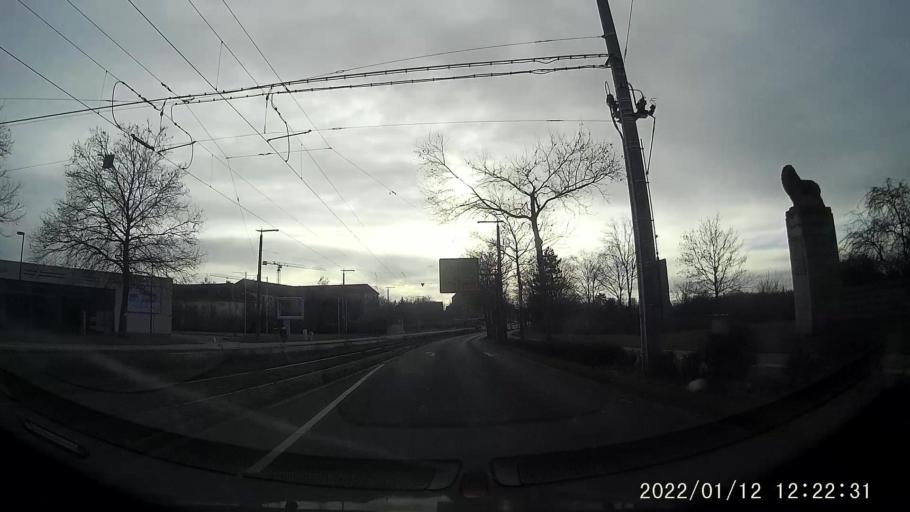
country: DE
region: Saxony
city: Goerlitz
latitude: 51.1937
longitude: 14.9478
